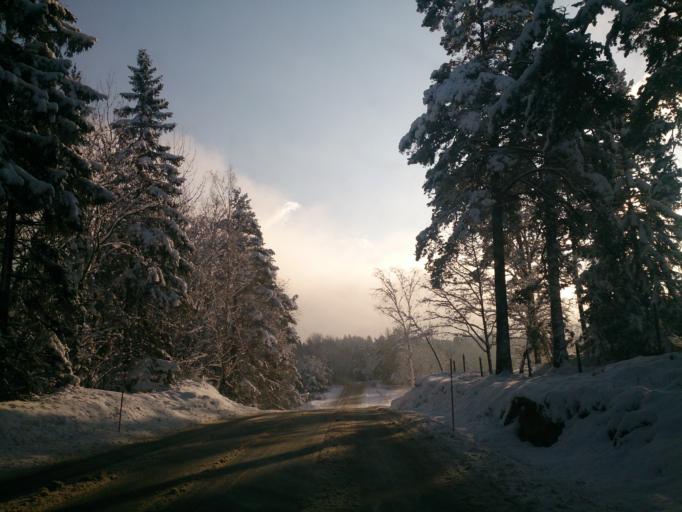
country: SE
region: Stockholm
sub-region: Varmdo Kommun
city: Holo
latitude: 59.2808
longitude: 18.6228
